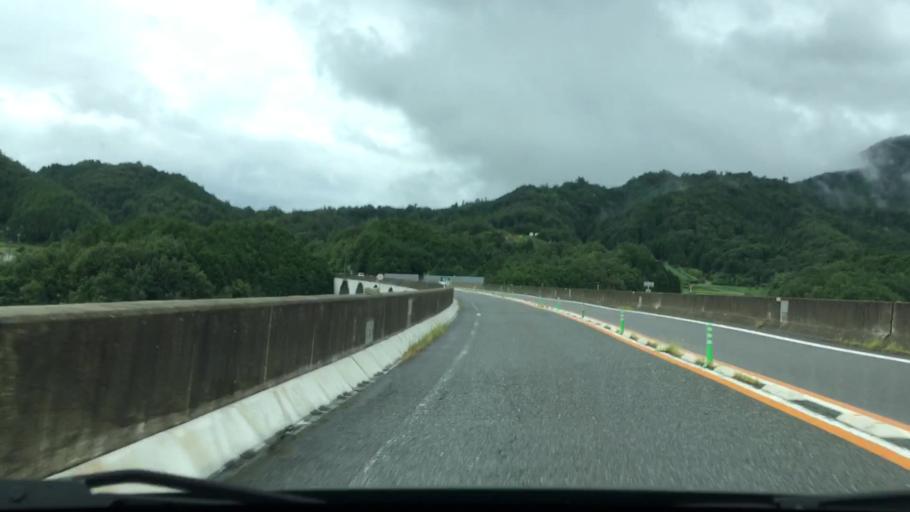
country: JP
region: Hyogo
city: Toyooka
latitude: 35.3102
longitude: 134.8270
